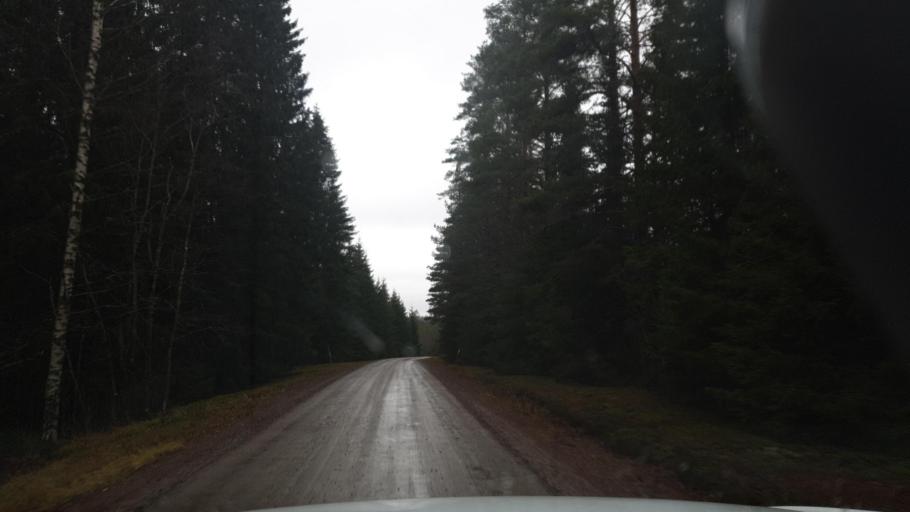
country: SE
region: Vaermland
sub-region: Arvika Kommun
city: Arvika
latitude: 59.8336
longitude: 12.6088
